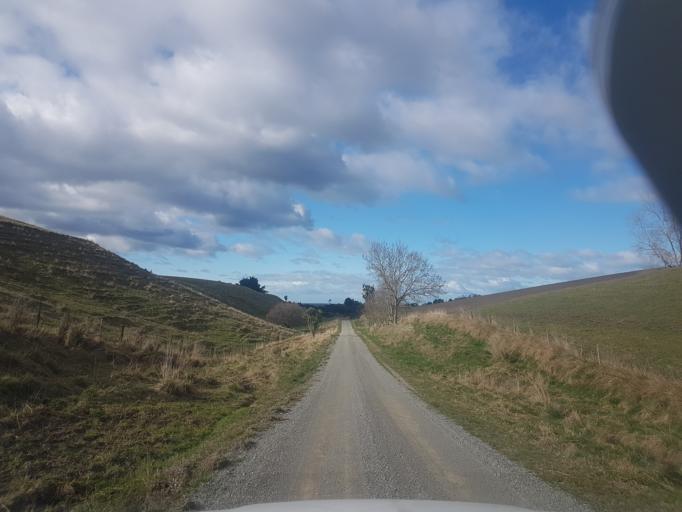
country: NZ
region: Canterbury
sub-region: Timaru District
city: Pleasant Point
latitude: -44.1833
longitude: 171.1302
